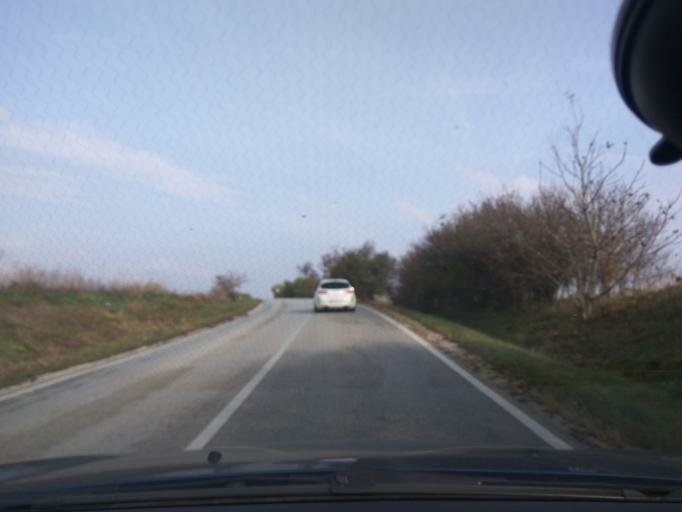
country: SK
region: Trnavsky
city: Vrbove
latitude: 48.6613
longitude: 17.7603
